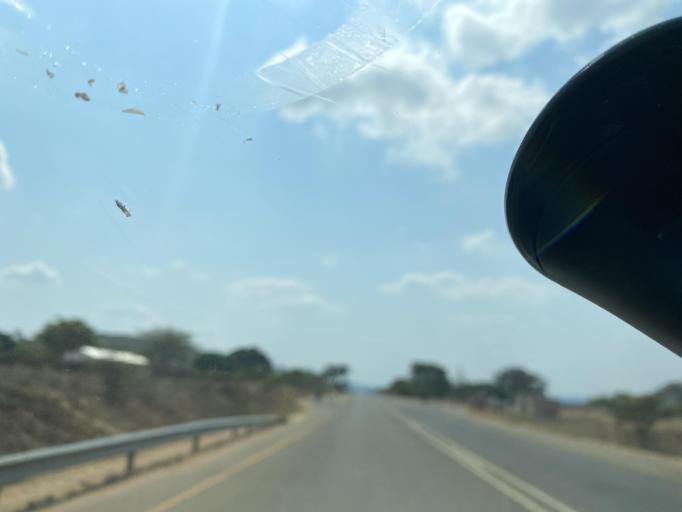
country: ZM
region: Lusaka
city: Chongwe
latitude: -15.6023
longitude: 28.7359
